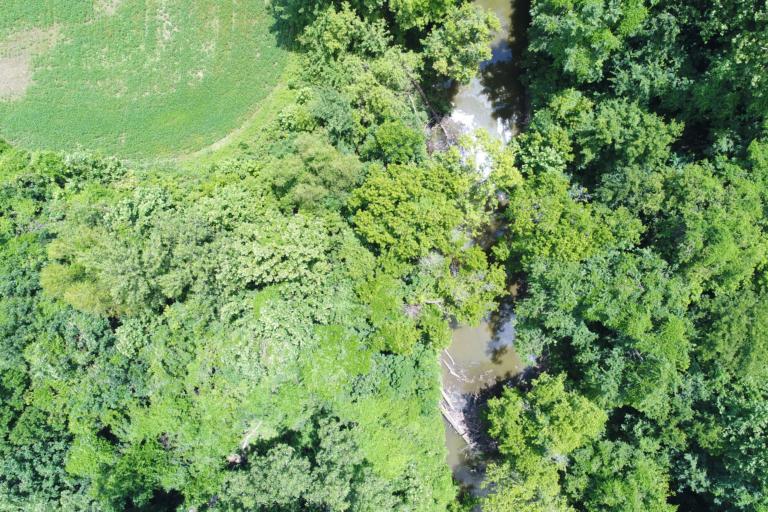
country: US
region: Mississippi
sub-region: De Soto County
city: Walls
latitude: 34.9190
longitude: -90.1841
